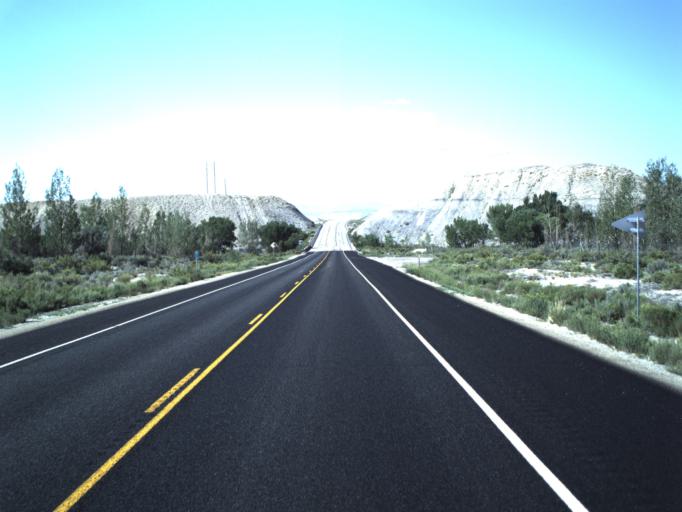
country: US
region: Utah
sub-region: Emery County
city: Ferron
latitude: 38.9560
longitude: -111.2031
